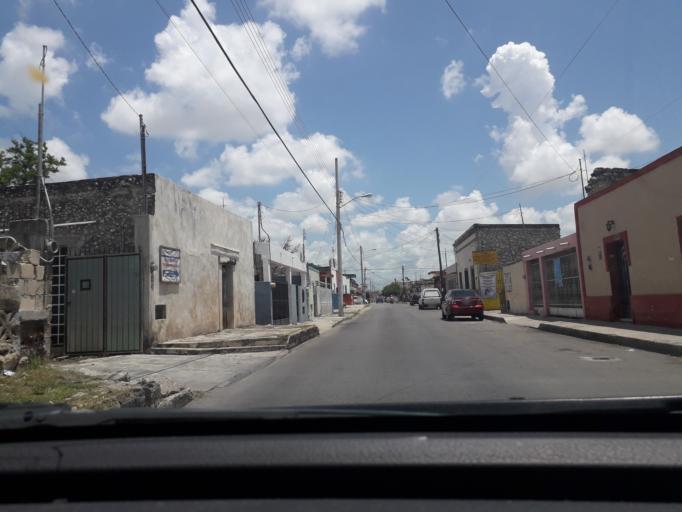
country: MX
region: Yucatan
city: Merida
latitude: 20.9539
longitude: -89.6208
